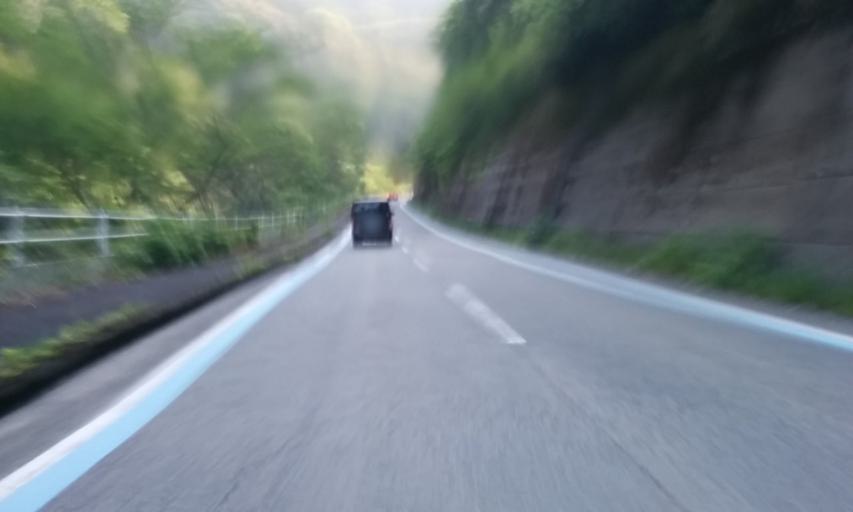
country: JP
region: Ehime
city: Saijo
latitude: 33.8657
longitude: 133.1879
